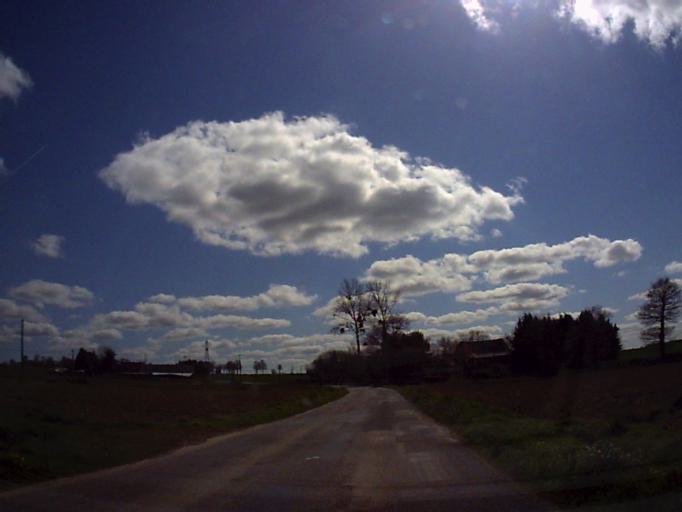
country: FR
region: Brittany
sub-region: Departement d'Ille-et-Vilaine
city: Saint-Meen-le-Grand
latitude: 48.1500
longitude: -2.1571
